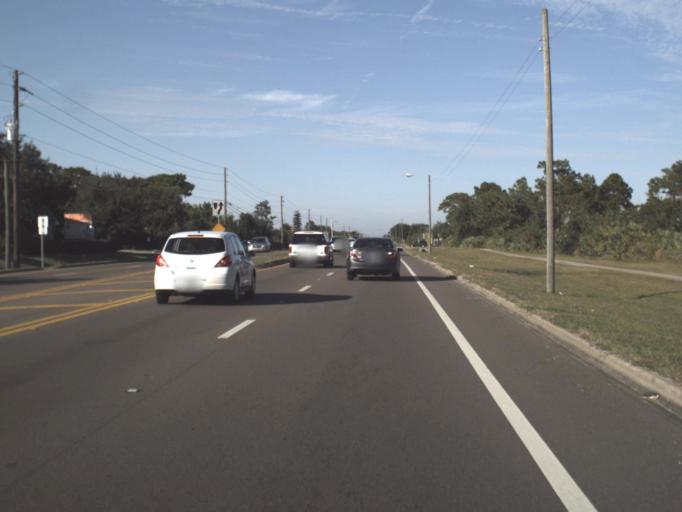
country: US
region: Florida
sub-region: Brevard County
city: South Patrick Shores
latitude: 28.1586
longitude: -80.6719
